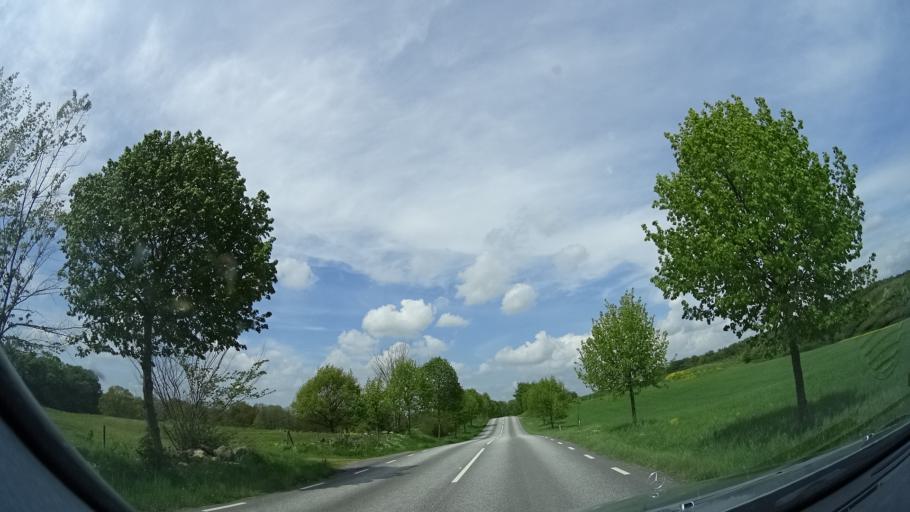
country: SE
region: Skane
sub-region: Sjobo Kommun
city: Sjoebo
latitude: 55.6703
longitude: 13.6656
